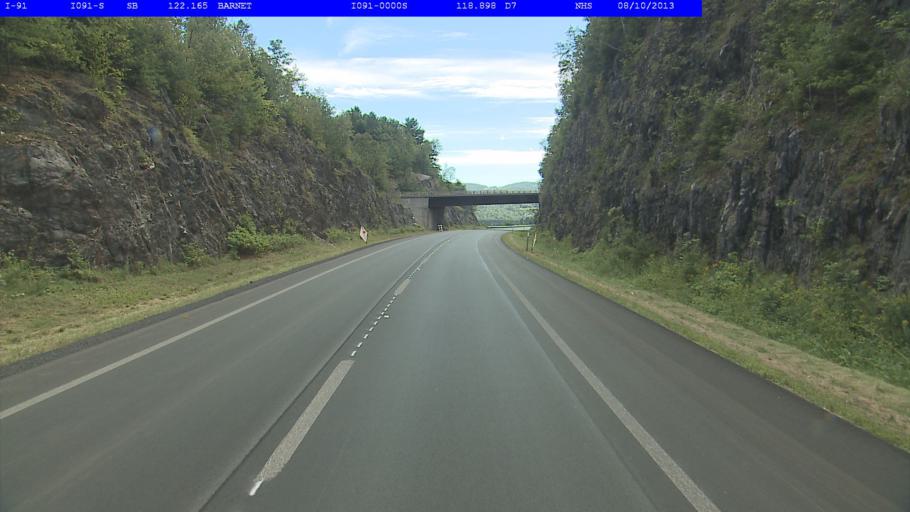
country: US
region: Vermont
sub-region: Caledonia County
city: Saint Johnsbury
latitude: 44.3132
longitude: -72.0363
